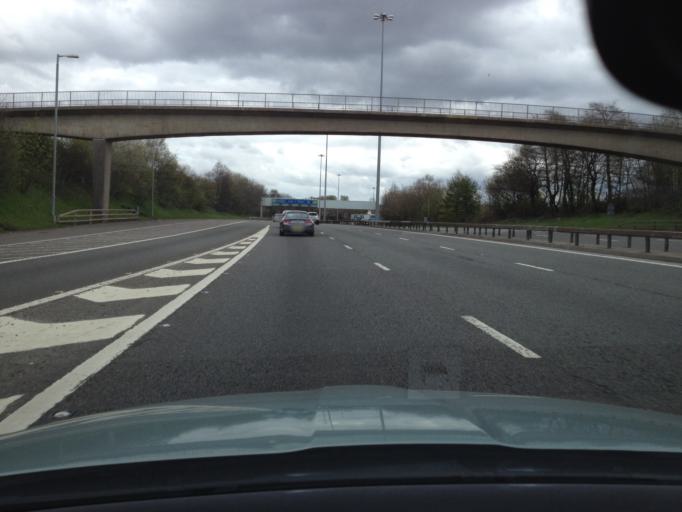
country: GB
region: Scotland
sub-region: East Dunbartonshire
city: Bishopbriggs
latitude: 55.8727
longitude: -4.1931
